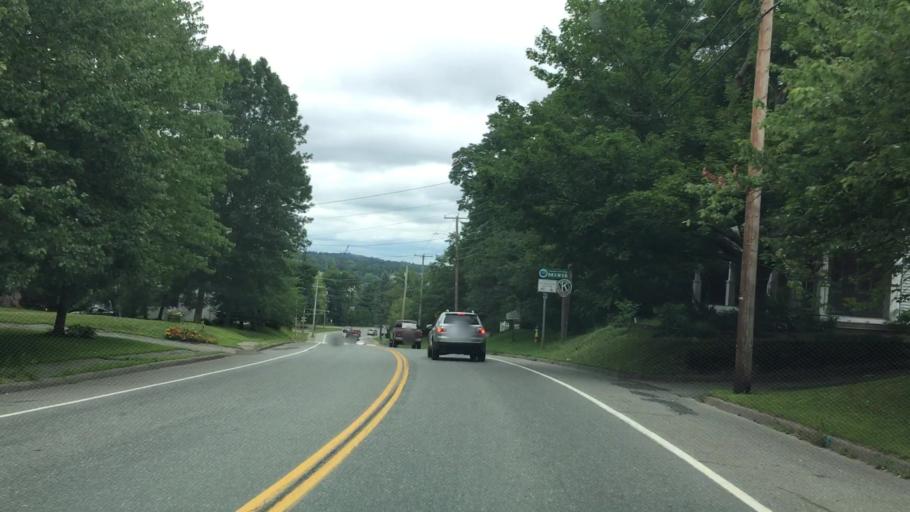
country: US
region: Maine
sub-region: Penobscot County
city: Bangor
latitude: 44.7654
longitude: -68.7835
